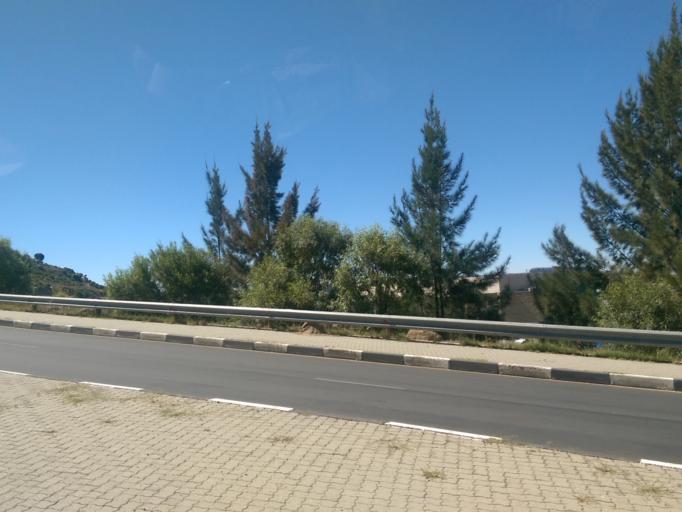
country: LS
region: Maseru
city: Maseru
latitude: -29.3254
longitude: 27.4979
